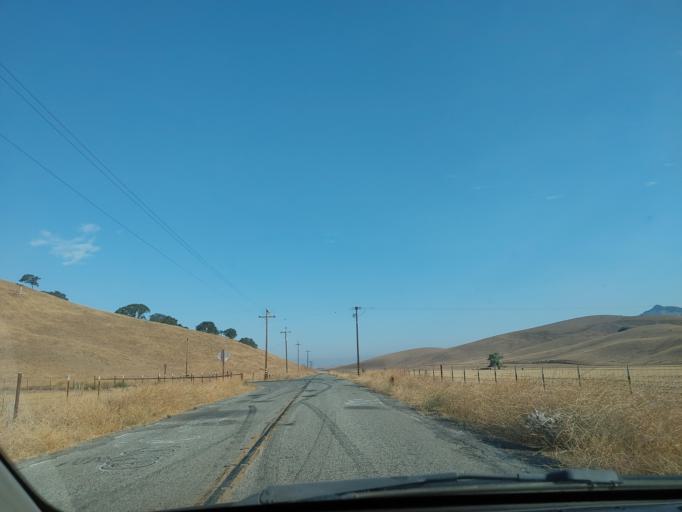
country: US
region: California
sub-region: San Benito County
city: Ridgemark
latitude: 36.8007
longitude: -121.2713
